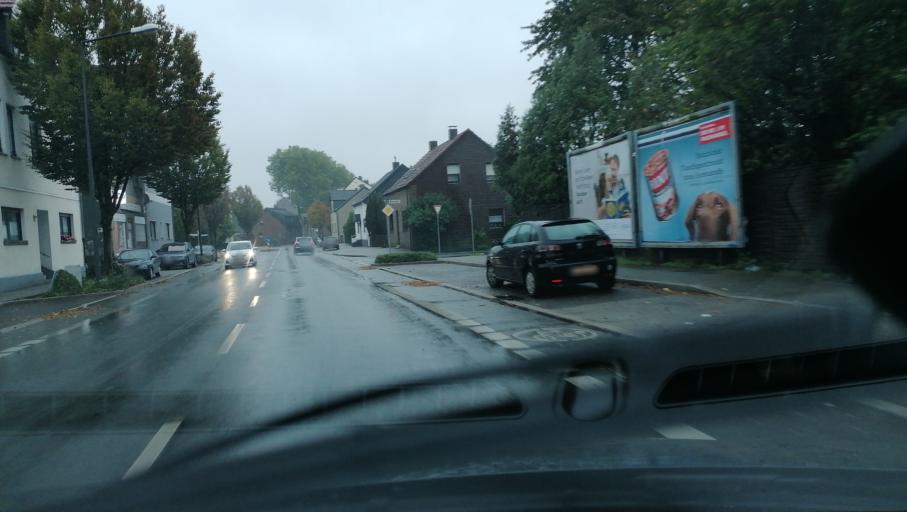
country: DE
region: North Rhine-Westphalia
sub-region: Regierungsbezirk Arnsberg
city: Herne
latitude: 51.5702
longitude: 7.2216
